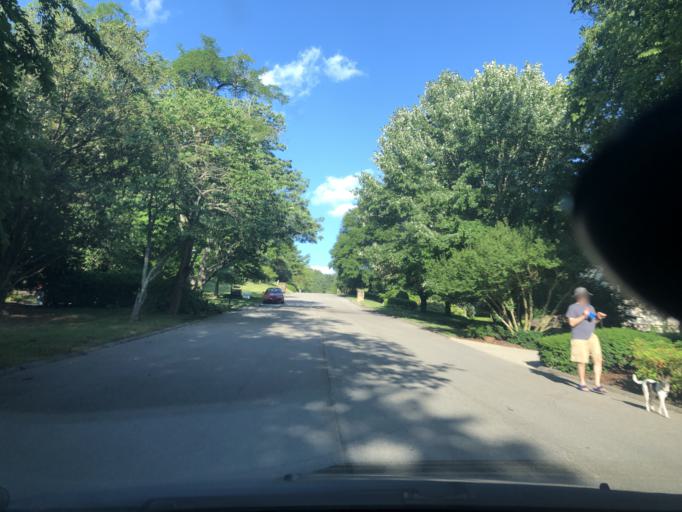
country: US
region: Tennessee
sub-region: Davidson County
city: Forest Hills
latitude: 36.0590
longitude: -86.8311
